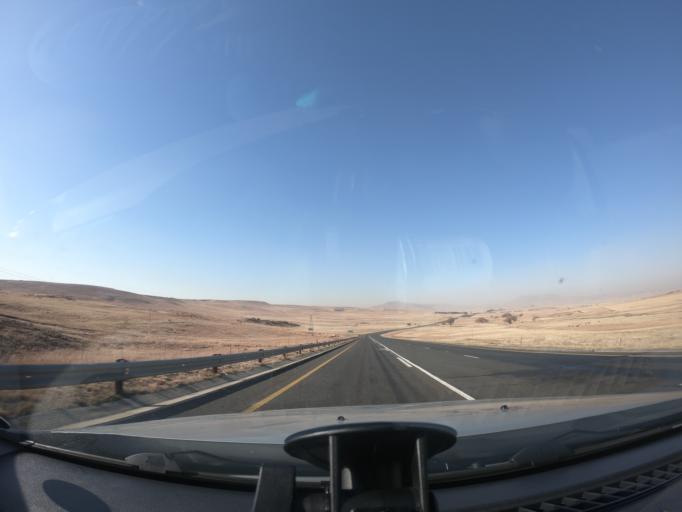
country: ZA
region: Mpumalanga
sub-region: Gert Sibande District Municipality
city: Volksrust
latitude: -27.2144
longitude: 29.8827
